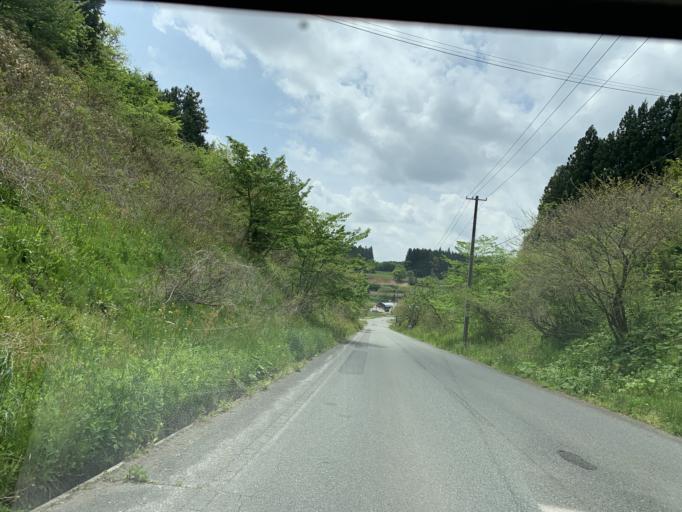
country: JP
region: Miyagi
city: Furukawa
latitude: 38.7335
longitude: 140.9272
